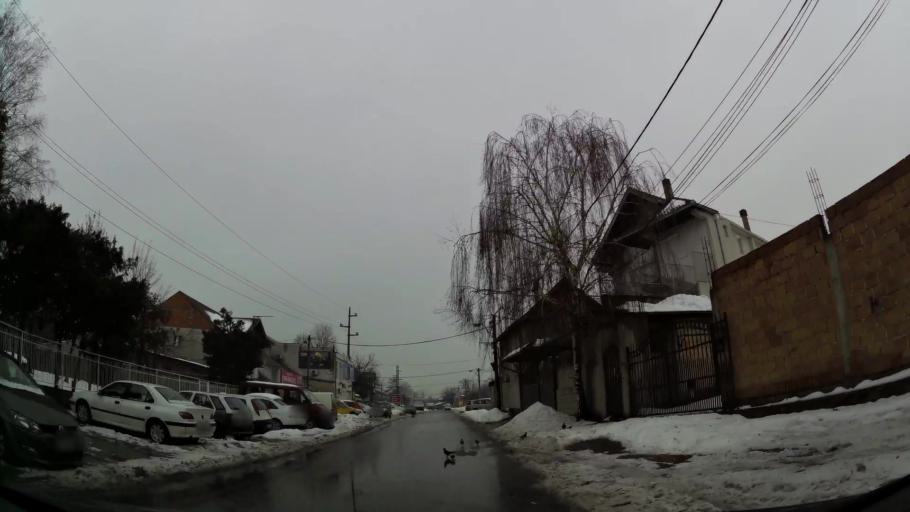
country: RS
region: Central Serbia
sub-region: Belgrade
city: Zemun
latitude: 44.8454
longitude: 20.3748
